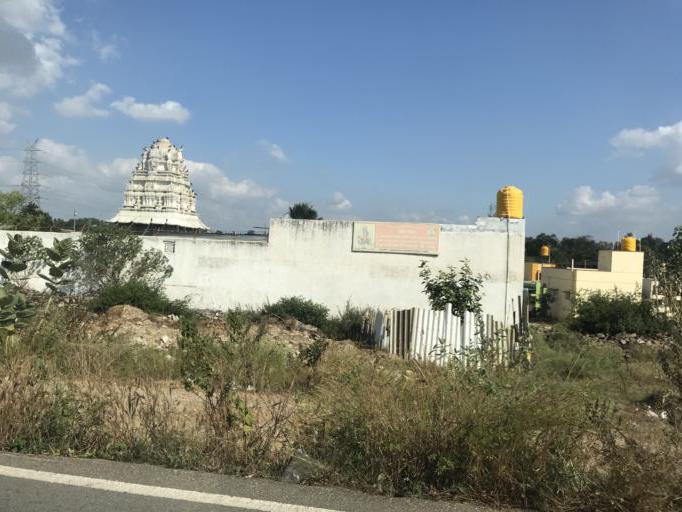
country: IN
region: Karnataka
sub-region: Bangalore Urban
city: Bangalore
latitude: 12.8192
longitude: 77.5772
